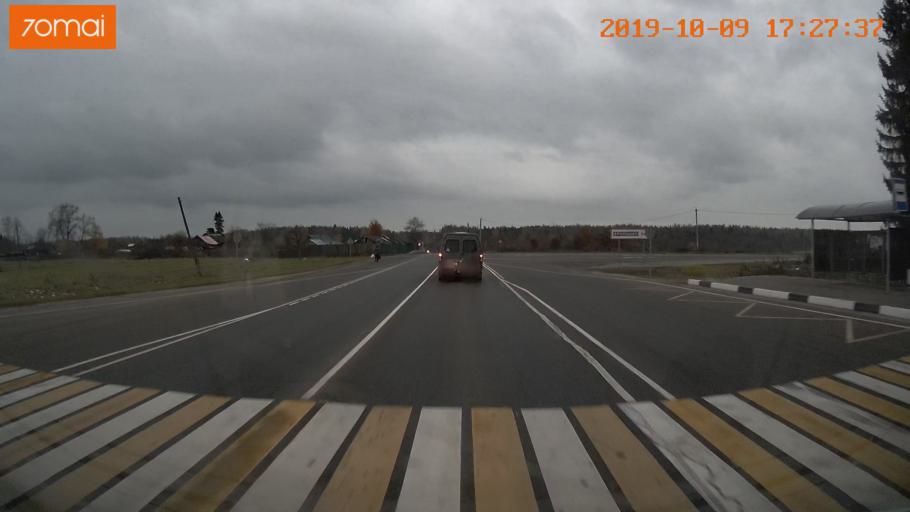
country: RU
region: Ivanovo
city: Furmanov
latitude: 57.1651
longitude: 41.0704
